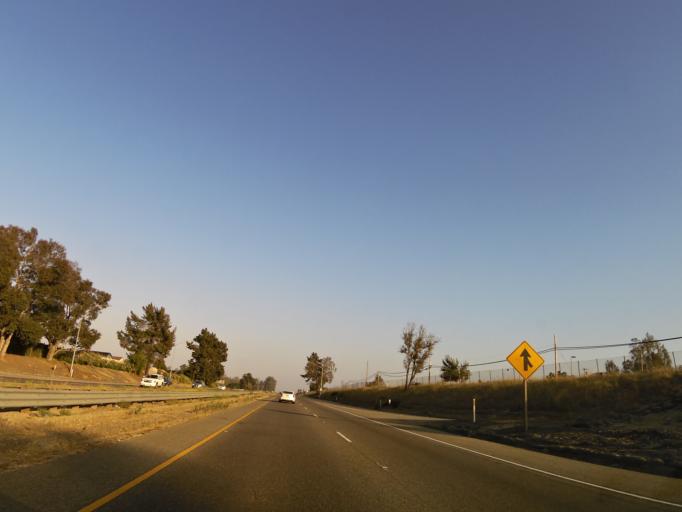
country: US
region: California
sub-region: San Luis Obispo County
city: Nipomo
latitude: 35.0360
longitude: -120.4839
